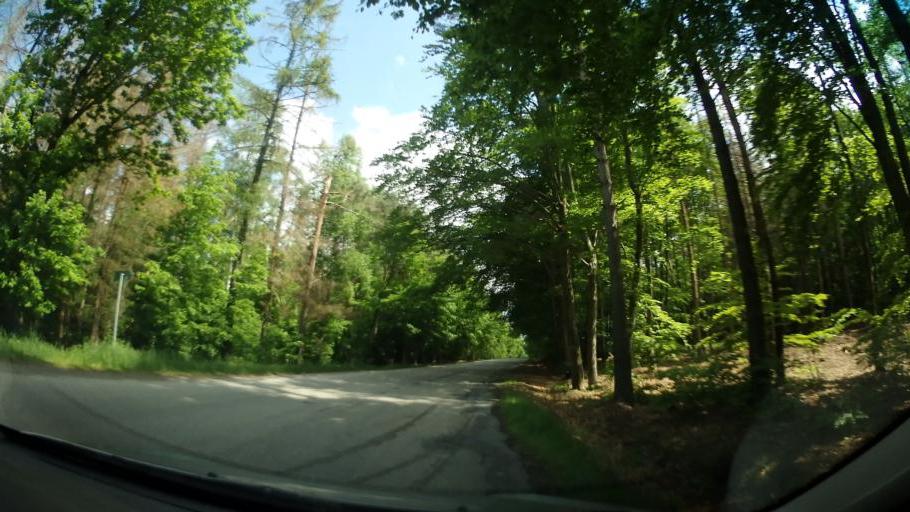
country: CZ
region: Vysocina
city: Mohelno
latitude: 49.1311
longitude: 16.1436
